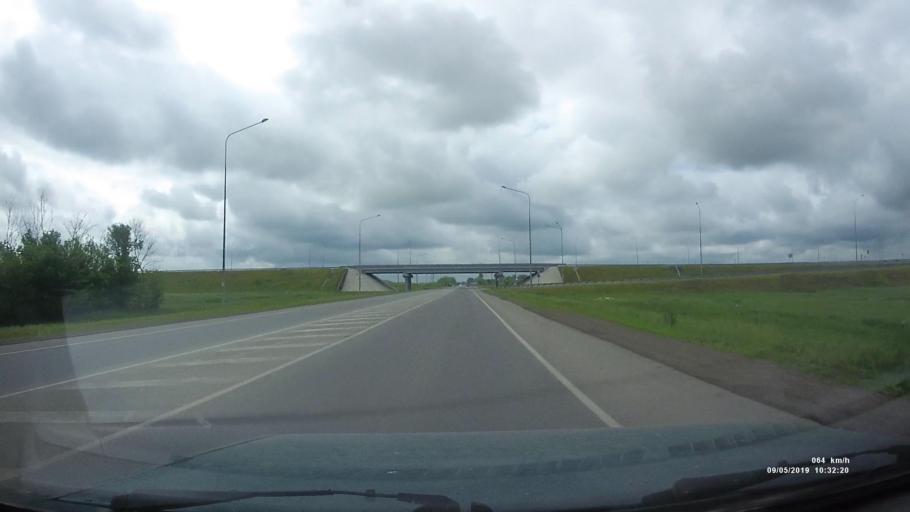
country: RU
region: Rostov
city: Azov
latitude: 47.0734
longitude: 39.4264
